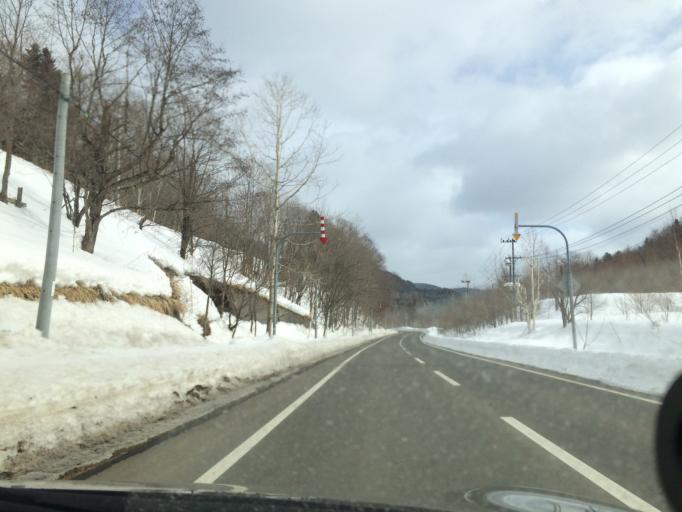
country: JP
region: Hokkaido
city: Shimo-furano
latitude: 43.0502
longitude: 142.5031
